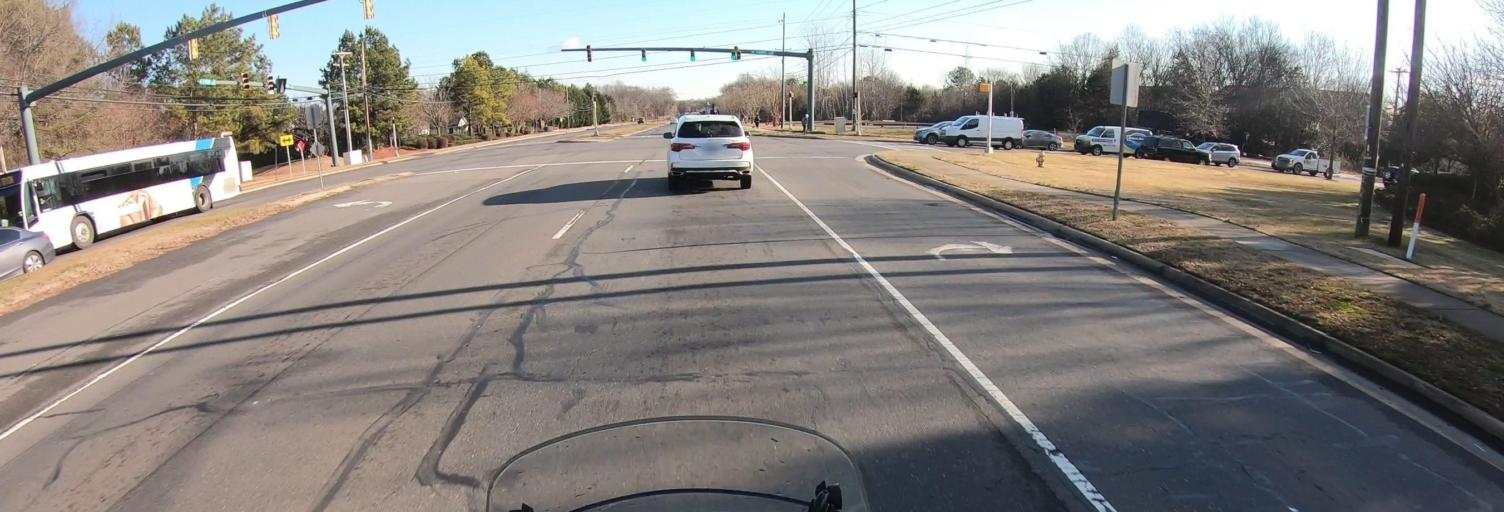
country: US
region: South Carolina
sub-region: York County
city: Lake Wylie
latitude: 35.1076
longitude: -80.9791
